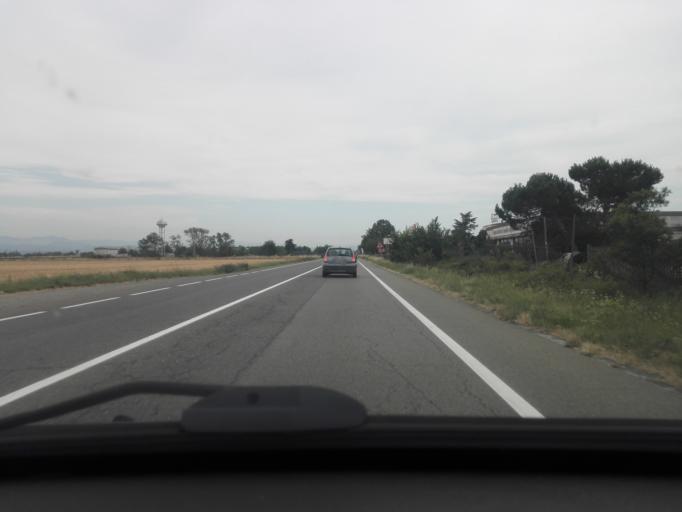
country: IT
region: Piedmont
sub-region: Provincia di Alessandria
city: Mandrogne
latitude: 44.8324
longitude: 8.7394
